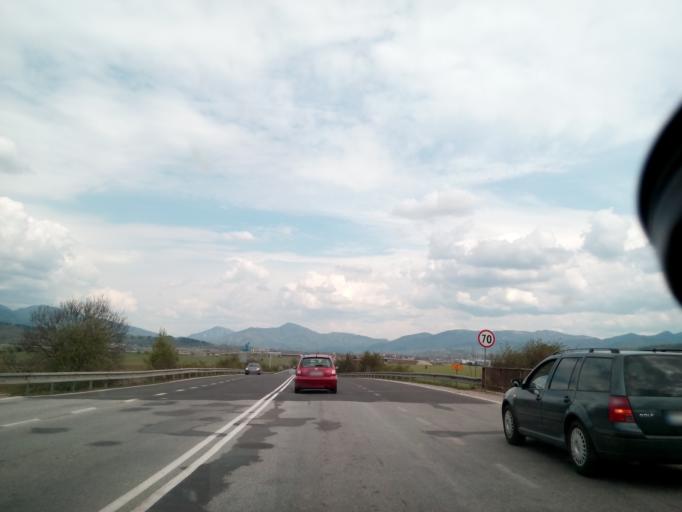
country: SK
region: Zilinsky
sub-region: Okres Zilina
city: Vrutky
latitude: 49.0930
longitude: 18.9356
